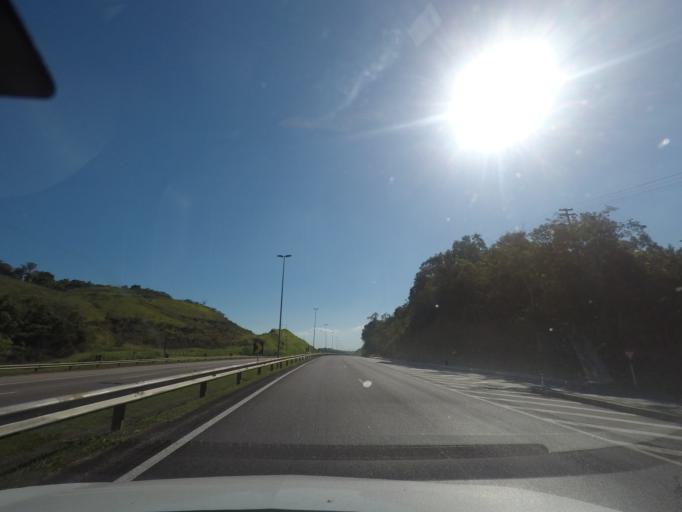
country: BR
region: Rio de Janeiro
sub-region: Guapimirim
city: Guapimirim
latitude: -22.6419
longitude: -43.0644
